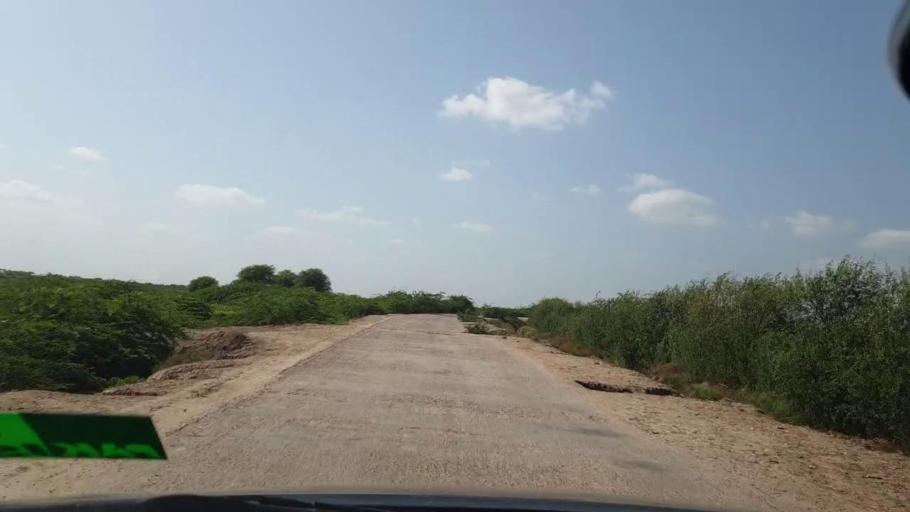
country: PK
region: Sindh
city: Tando Bago
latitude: 24.6652
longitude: 69.1984
